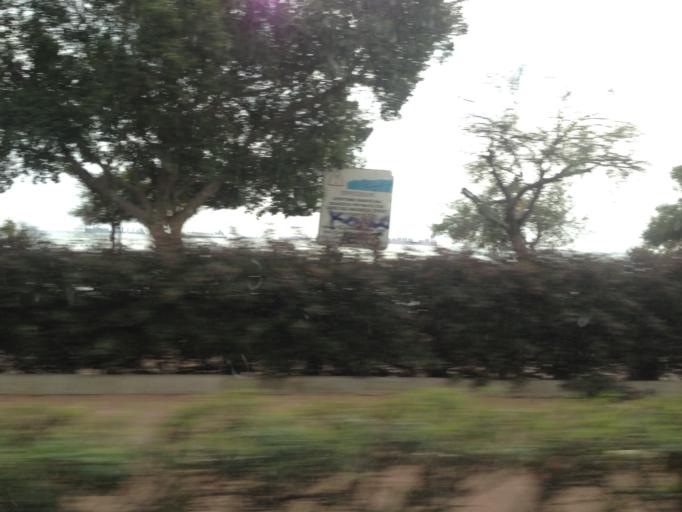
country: CY
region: Limassol
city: Limassol
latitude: 34.6838
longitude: 33.0593
